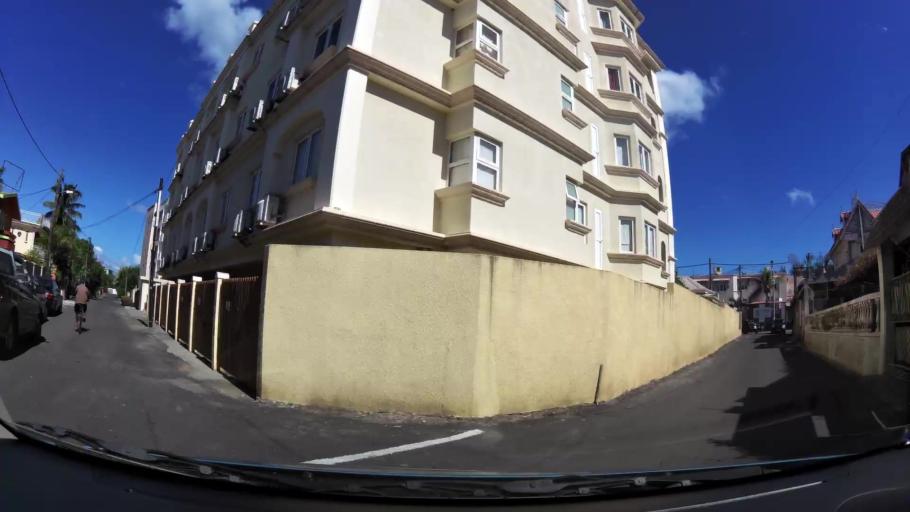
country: MU
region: Black River
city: Flic en Flac
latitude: -20.2792
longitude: 57.3692
